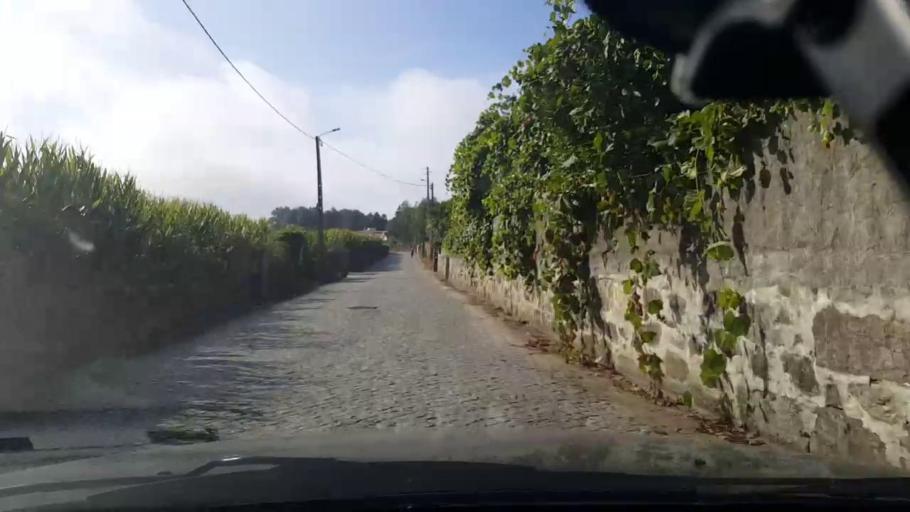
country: PT
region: Porto
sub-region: Maia
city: Gemunde
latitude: 41.2682
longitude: -8.6751
